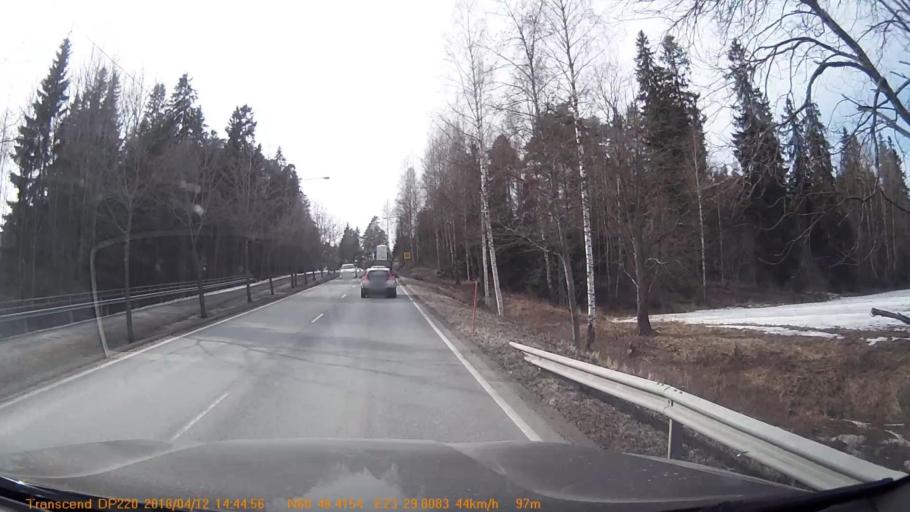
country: FI
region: Haeme
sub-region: Forssa
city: Jokioinen
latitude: 60.8069
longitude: 23.4965
